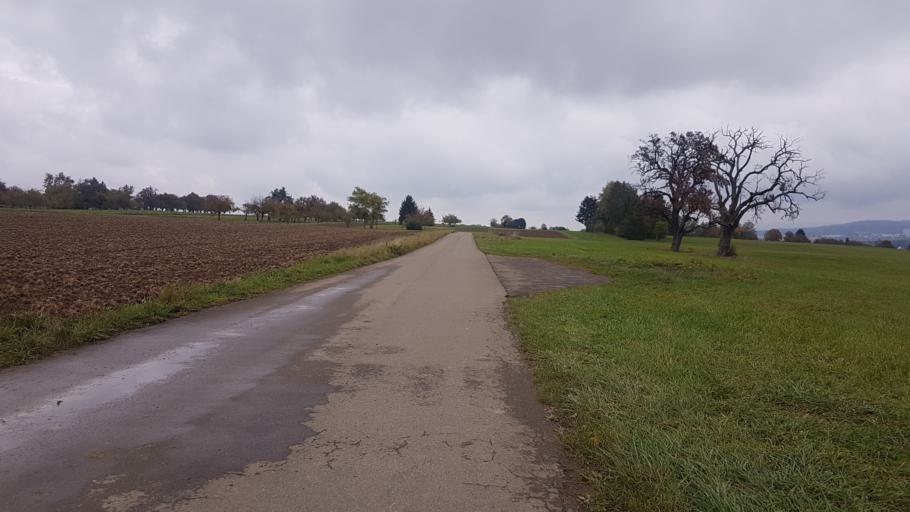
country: DE
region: Baden-Wuerttemberg
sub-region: Tuebingen Region
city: Dusslingen
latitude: 48.4521
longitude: 9.0330
